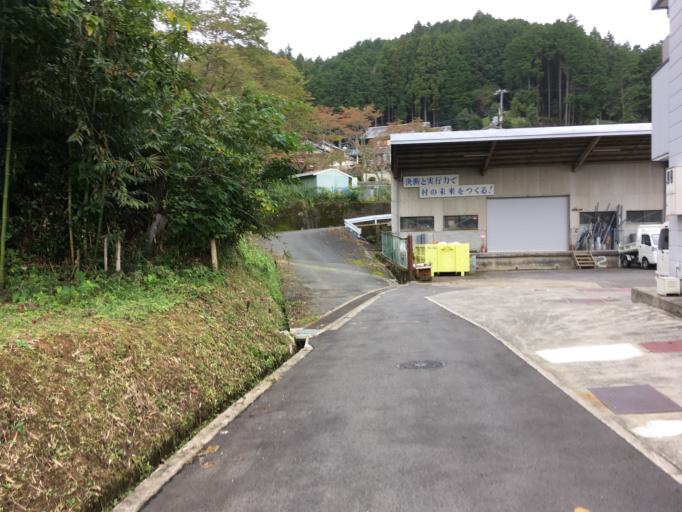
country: JP
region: Nara
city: Haibara-akanedai
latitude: 34.5644
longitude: 136.0106
